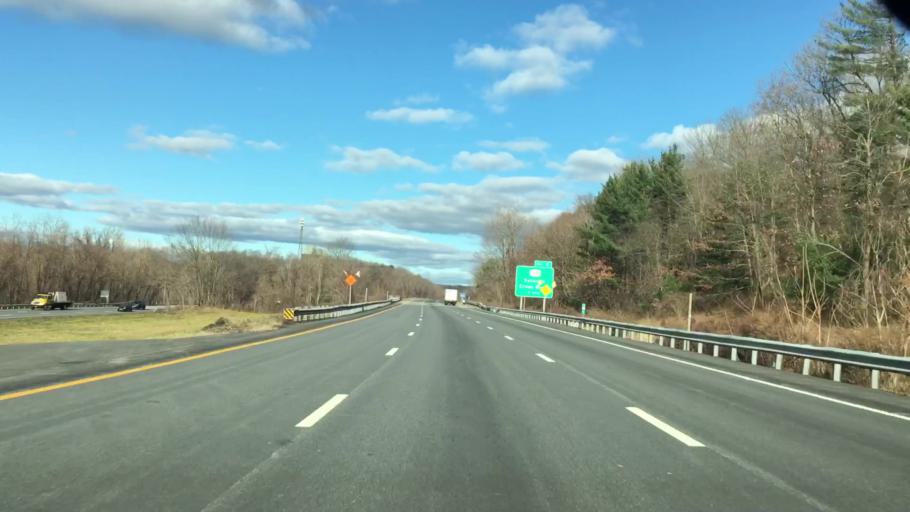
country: US
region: New York
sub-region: Westchester County
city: Bedford Hills
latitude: 41.2381
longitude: -73.6757
